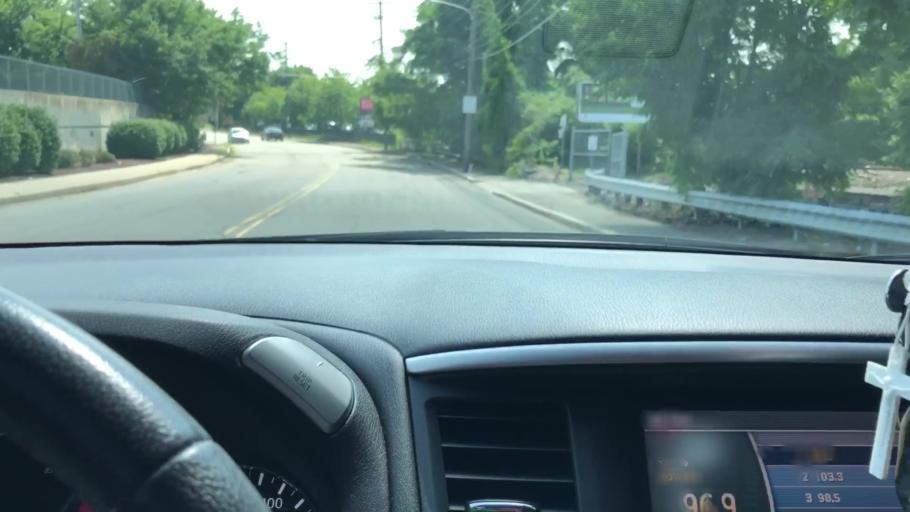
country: US
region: Rhode Island
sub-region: Providence County
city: Providence
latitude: 41.8457
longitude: -71.4135
